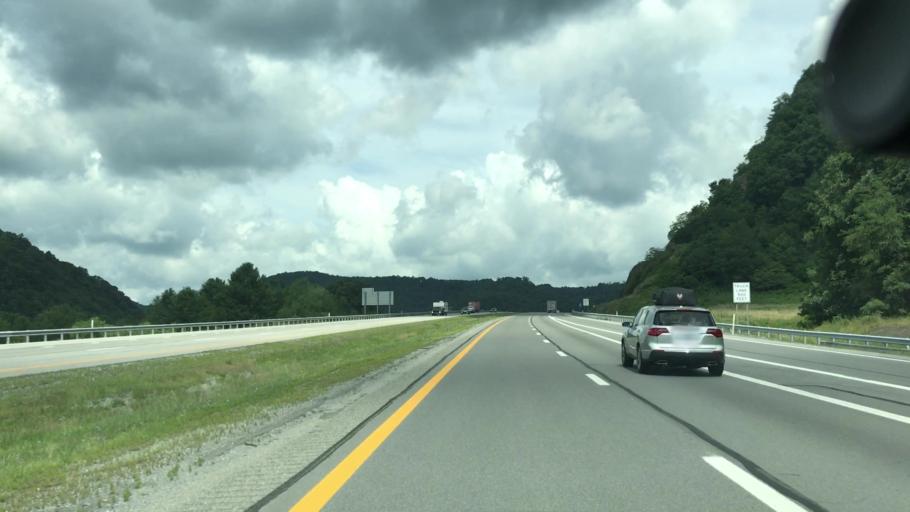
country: US
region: West Virginia
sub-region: Mercer County
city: Athens
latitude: 37.4985
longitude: -81.1073
